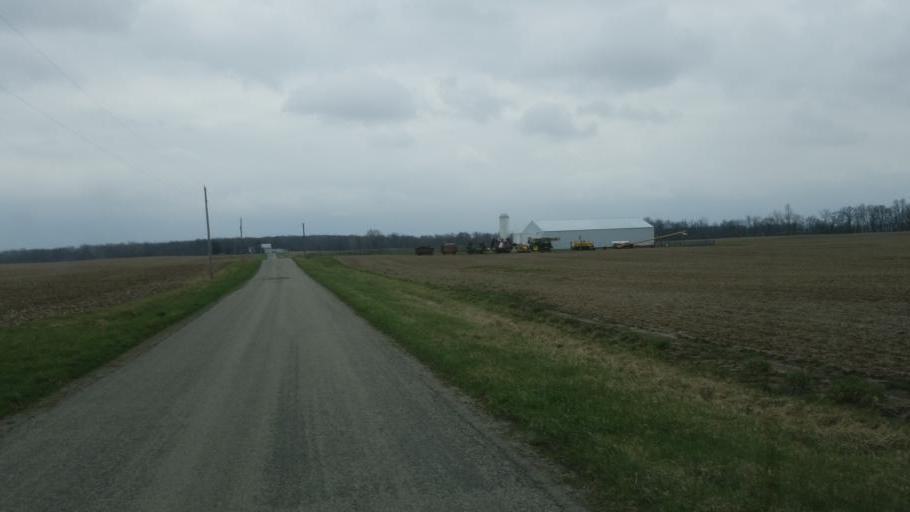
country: US
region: Ohio
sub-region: Union County
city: Richwood
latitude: 40.4166
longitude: -83.3641
